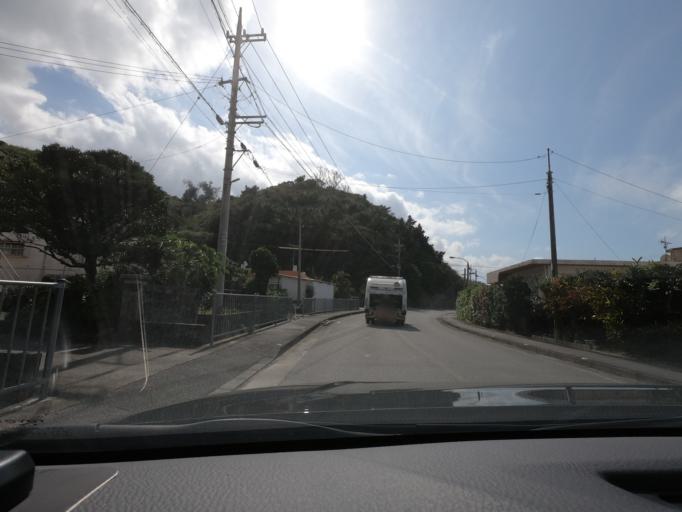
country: JP
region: Okinawa
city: Nago
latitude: 26.7561
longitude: 128.1891
